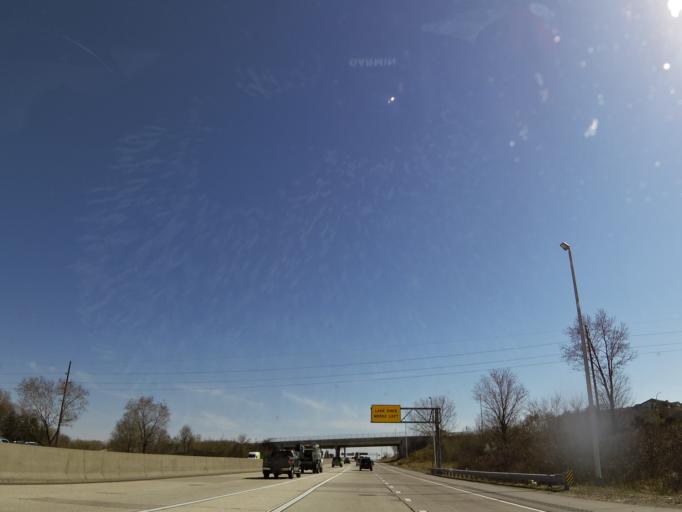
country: US
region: Minnesota
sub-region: Dakota County
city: Burnsville
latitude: 44.7327
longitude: -93.2836
